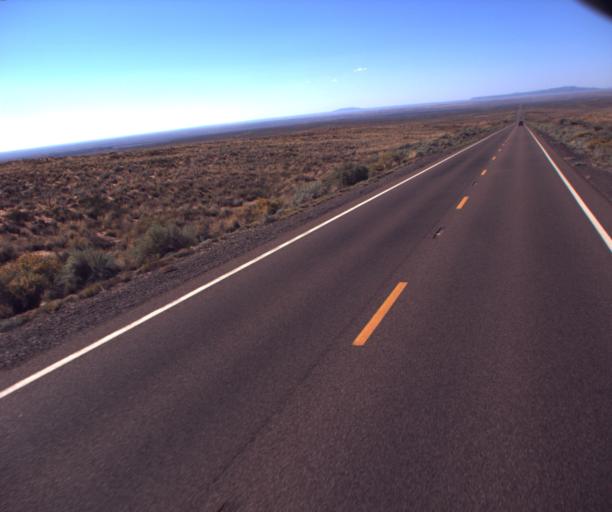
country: US
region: Arizona
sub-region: Navajo County
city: Winslow
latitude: 35.0657
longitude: -110.5782
